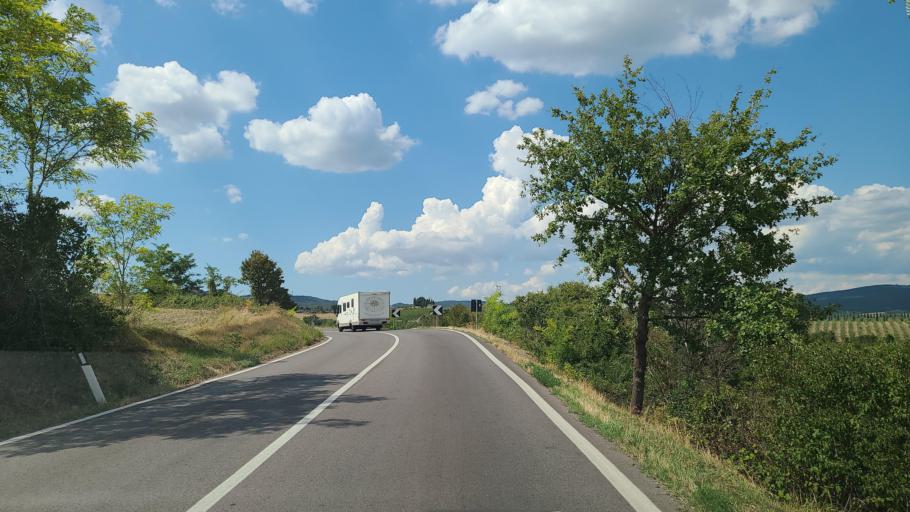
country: IT
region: Tuscany
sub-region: Provincia di Siena
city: Casole d'Elsa
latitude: 43.4030
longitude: 11.0346
